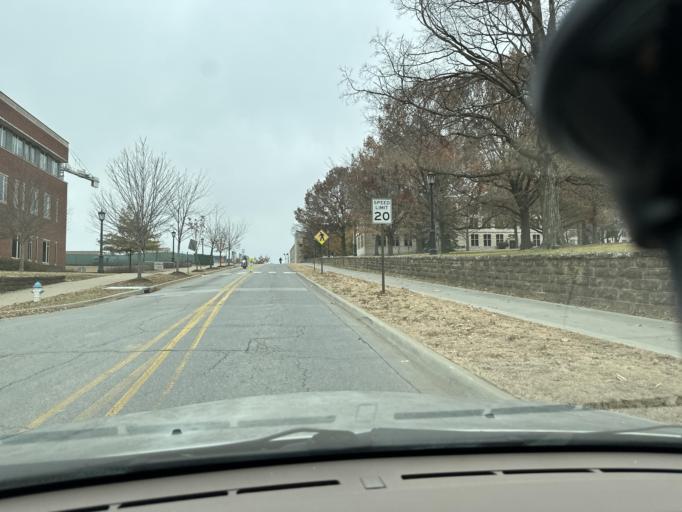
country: US
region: Arkansas
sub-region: Washington County
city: Fayetteville
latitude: 36.0666
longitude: -94.1689
